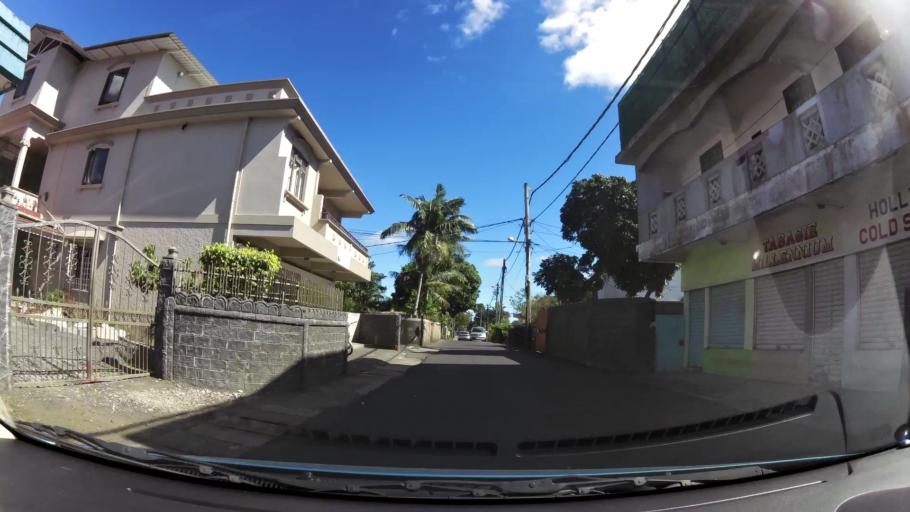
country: MU
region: Plaines Wilhems
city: Vacoas
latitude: -20.3139
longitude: 57.4808
